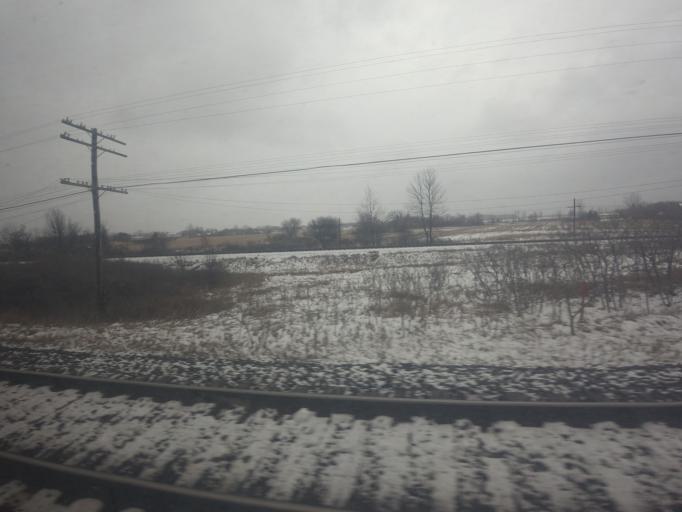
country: CA
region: Ontario
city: Quinte West
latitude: 44.0909
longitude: -77.6295
